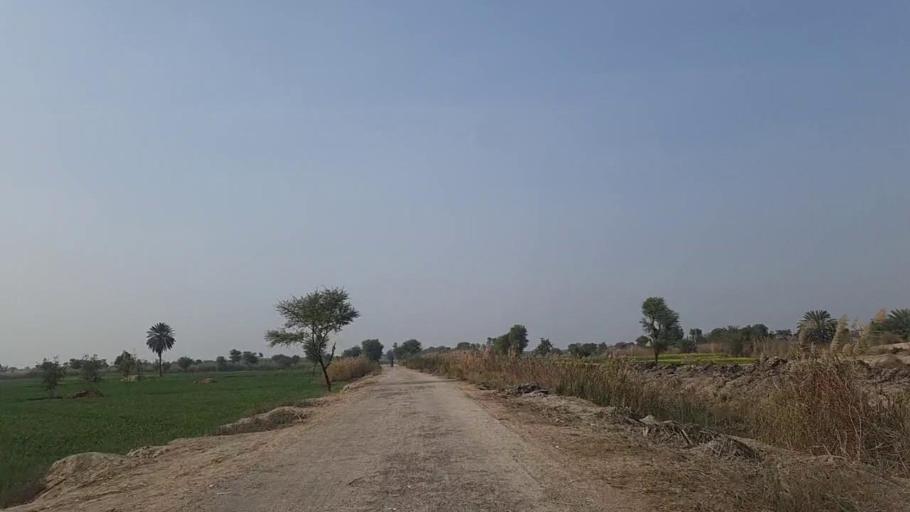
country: PK
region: Sindh
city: Daur
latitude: 26.5055
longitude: 68.4383
